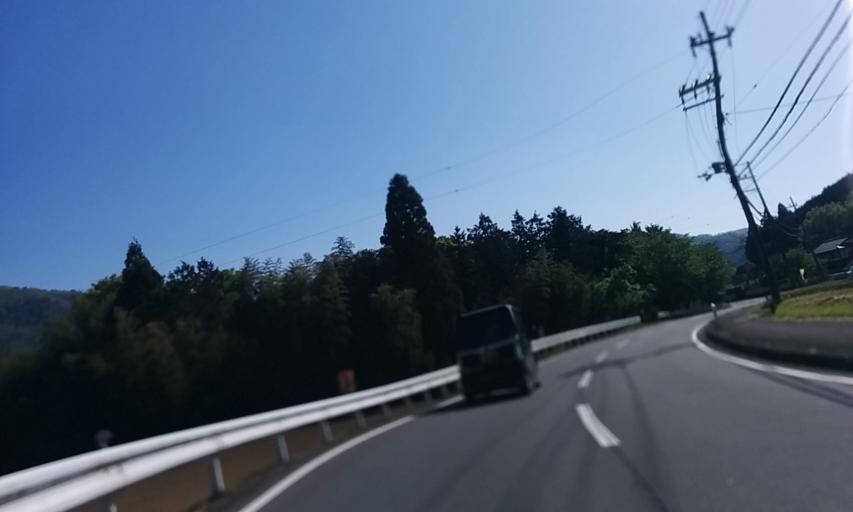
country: JP
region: Kyoto
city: Ayabe
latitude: 35.2556
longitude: 135.4247
